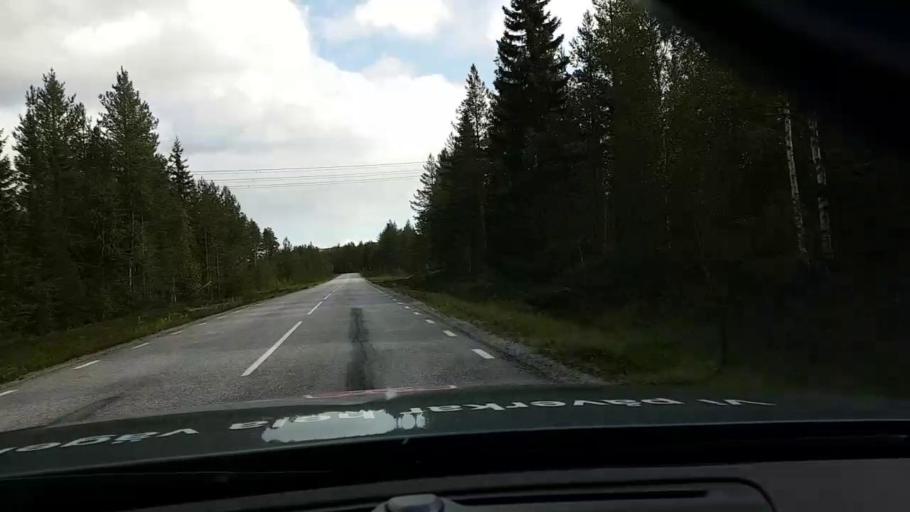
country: SE
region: Vaesternorrland
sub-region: OErnskoeldsviks Kommun
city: Bredbyn
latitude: 63.6759
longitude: 17.7944
